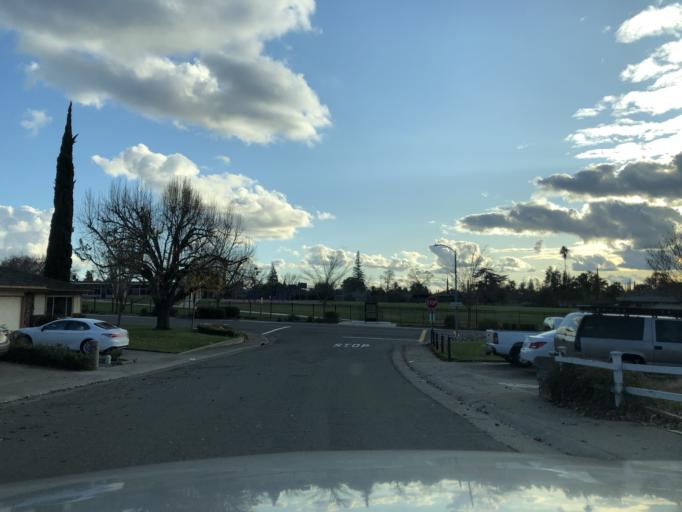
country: US
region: California
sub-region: Sacramento County
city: Foothill Farms
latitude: 38.6612
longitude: -121.3180
